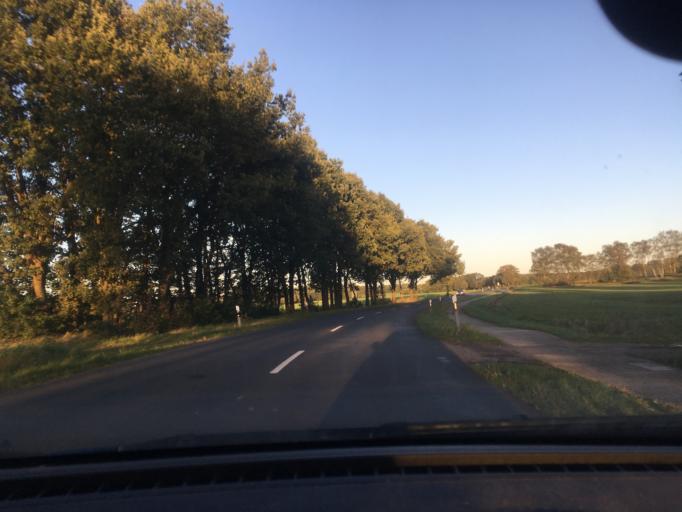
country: DE
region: Lower Saxony
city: Wendisch Evern
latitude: 53.2074
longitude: 10.4528
